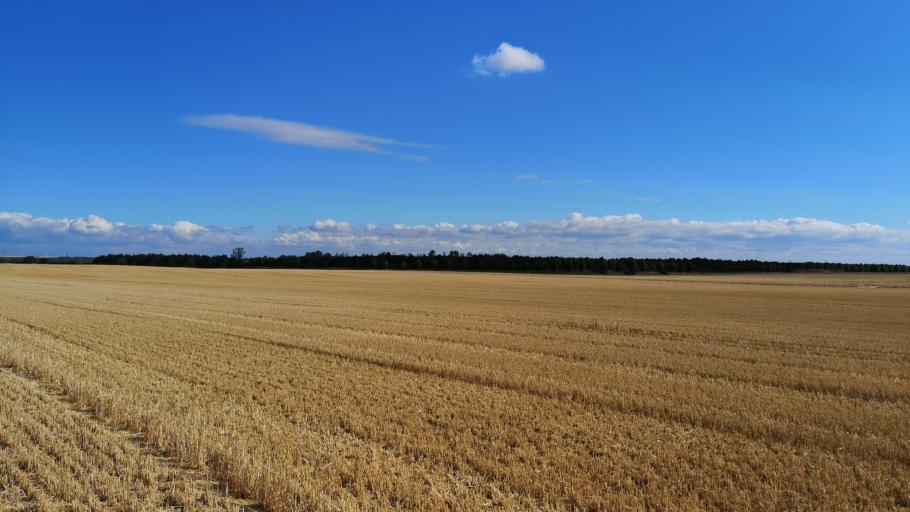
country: DE
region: Saxony-Anhalt
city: Laucha
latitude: 51.2555
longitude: 11.6806
